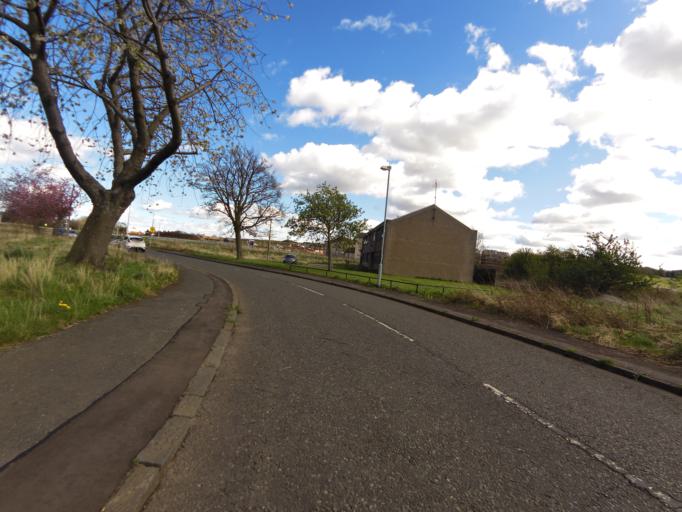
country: GB
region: Scotland
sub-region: West Lothian
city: Seafield
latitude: 55.9265
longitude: -3.1270
